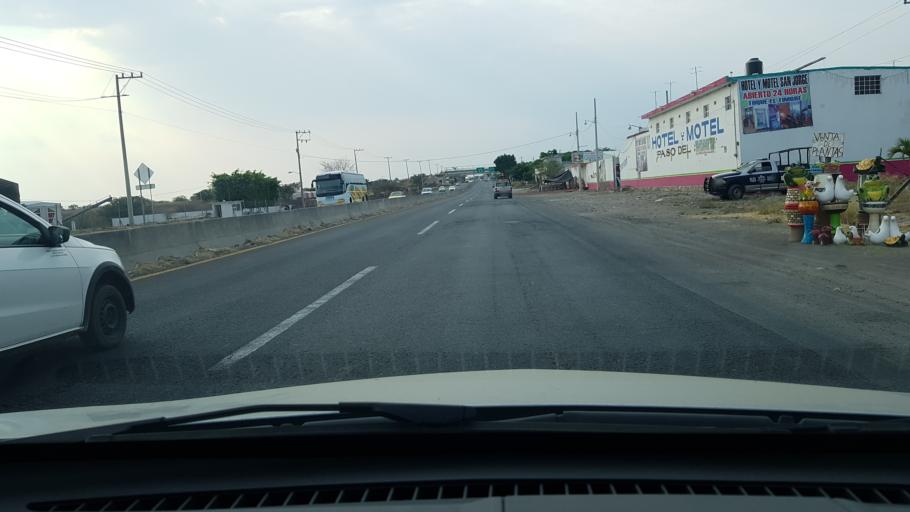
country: MX
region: Morelos
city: Amayuca
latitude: 18.7260
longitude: -98.8076
